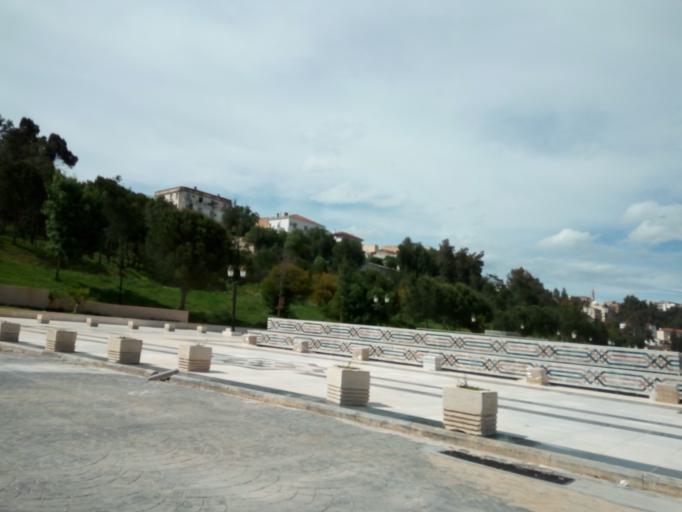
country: DZ
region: Constantine
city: Constantine
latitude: 36.3485
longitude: 6.6042
